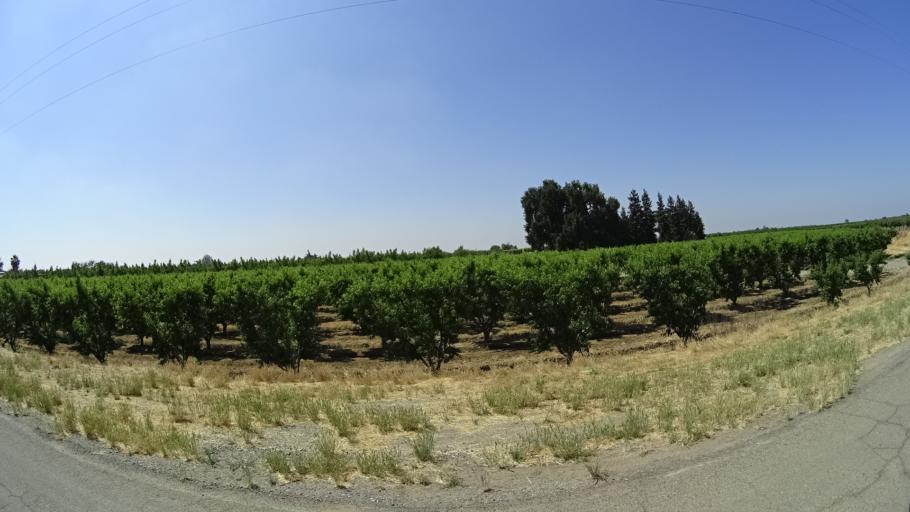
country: US
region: California
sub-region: Fresno County
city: Kingsburg
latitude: 36.4743
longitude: -119.5549
